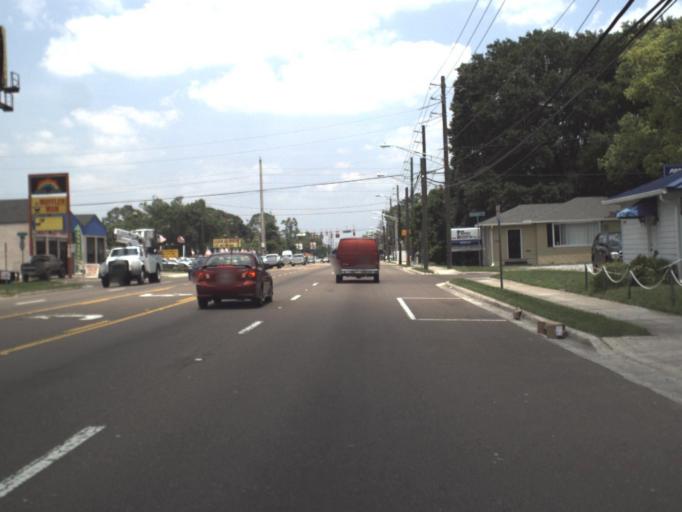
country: US
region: Florida
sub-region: Duval County
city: Jacksonville
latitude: 30.3013
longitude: -81.7304
